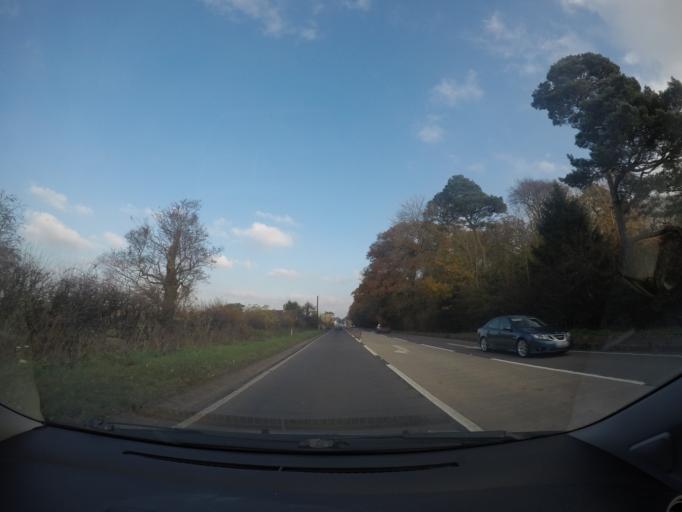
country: GB
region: England
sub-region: City of York
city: Holtby
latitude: 54.0131
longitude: -0.9898
